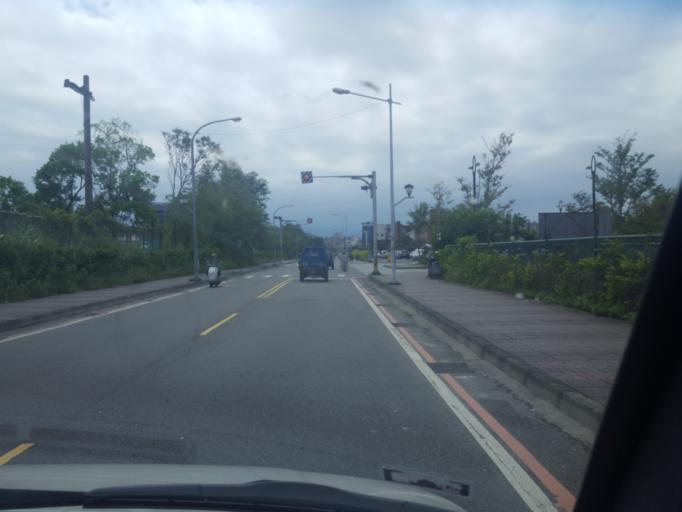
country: TW
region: Taiwan
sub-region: Yilan
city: Yilan
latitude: 24.7548
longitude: 121.7596
